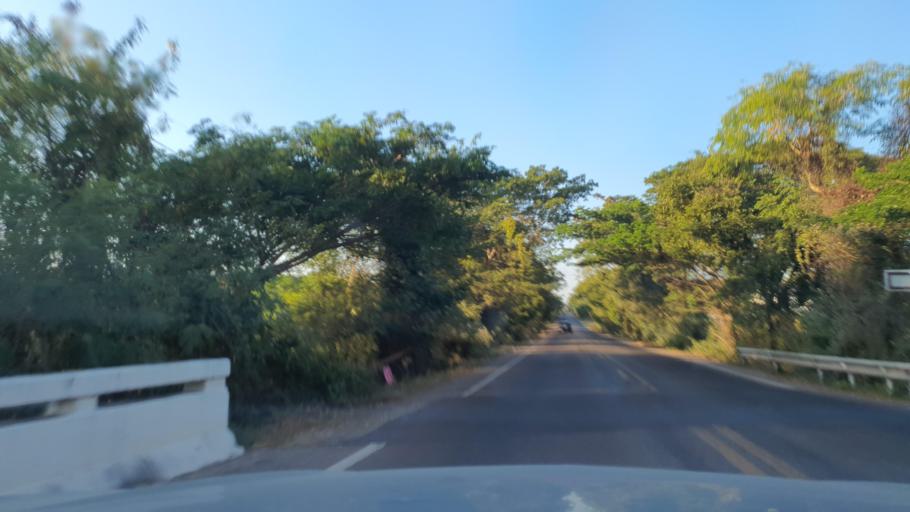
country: TH
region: Nakhon Phanom
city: Si Songkhram
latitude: 17.5664
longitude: 104.2349
